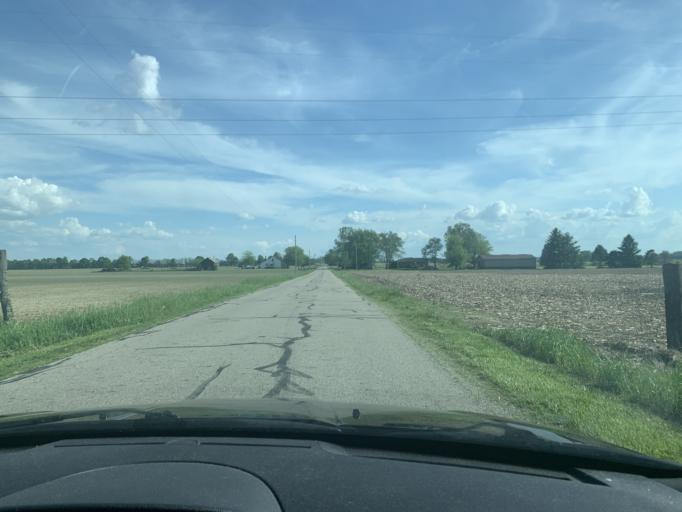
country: US
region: Ohio
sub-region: Logan County
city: De Graff
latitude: 40.2664
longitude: -84.0155
